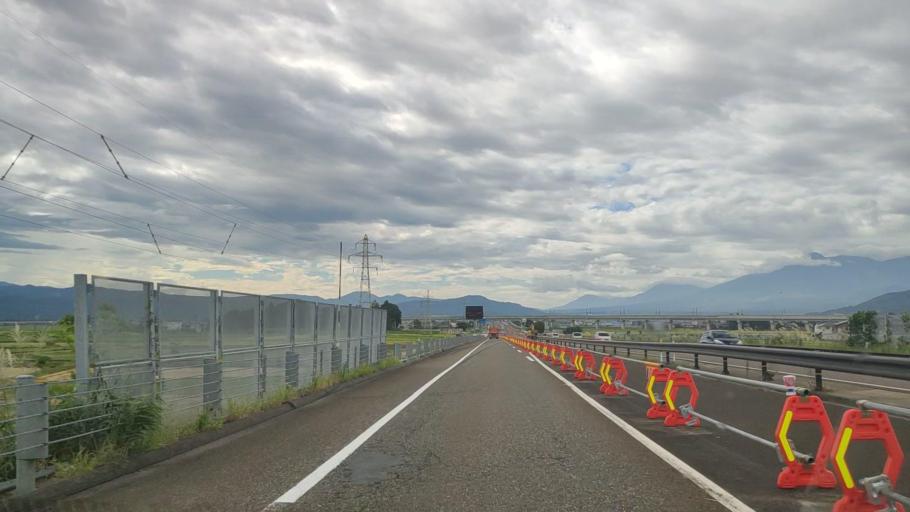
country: JP
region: Niigata
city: Joetsu
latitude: 37.0763
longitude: 138.2655
